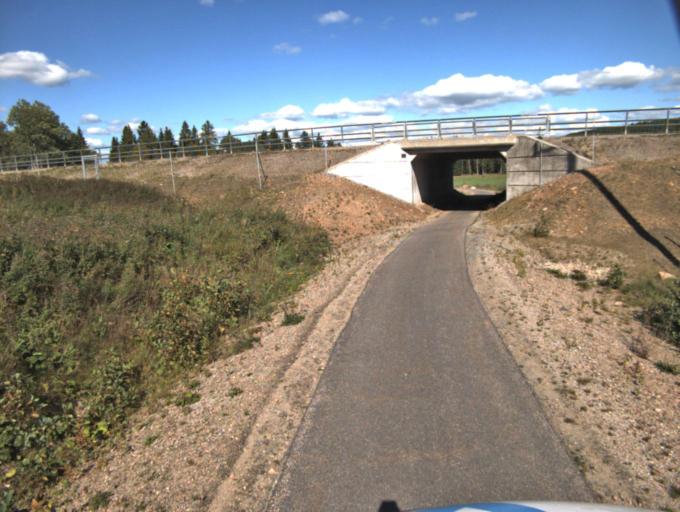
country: SE
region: Vaestra Goetaland
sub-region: Ulricehamns Kommun
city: Ulricehamn
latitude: 57.8149
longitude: 13.3539
